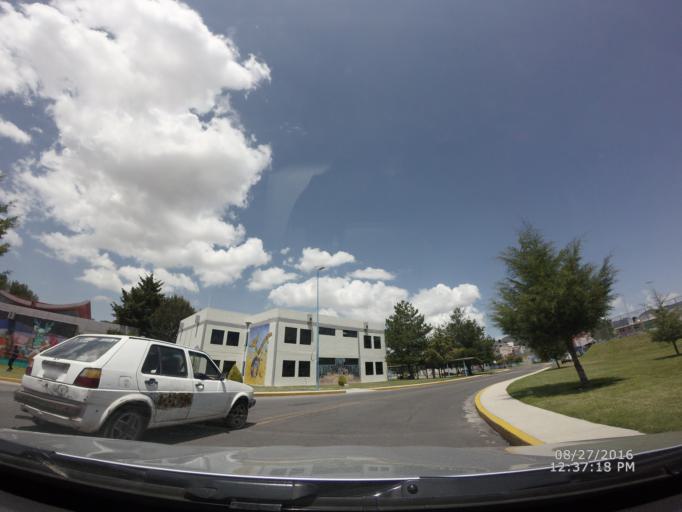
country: MX
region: Hidalgo
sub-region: Mineral de la Reforma
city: Campestre Villas del Alamo
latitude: 20.0953
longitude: -98.7106
